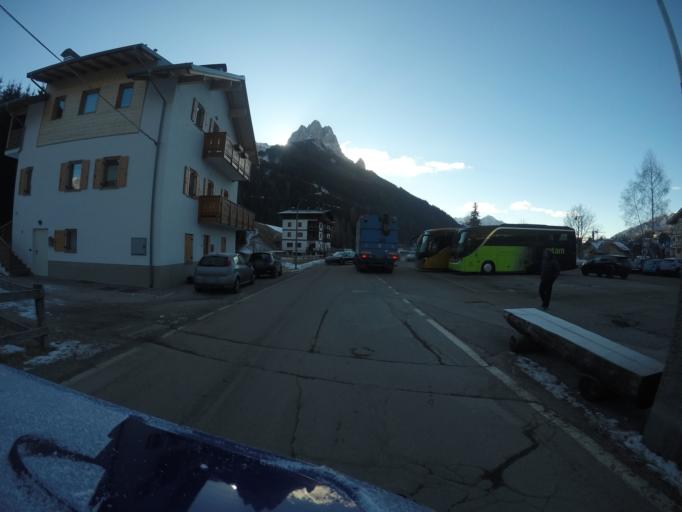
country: IT
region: Trentino-Alto Adige
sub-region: Provincia di Trento
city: Pozza di Fassa
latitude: 46.4292
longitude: 11.6868
